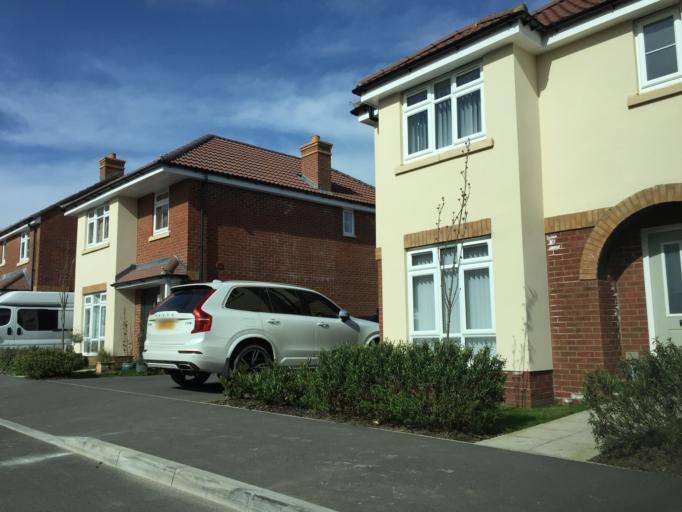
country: GB
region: England
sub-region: Wiltshire
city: Chippenham
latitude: 51.4635
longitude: -2.1323
